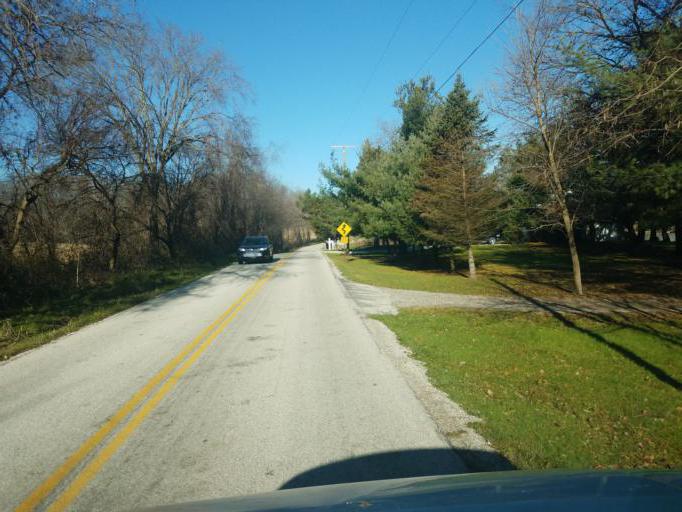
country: US
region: Ohio
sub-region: Richland County
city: Lincoln Heights
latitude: 40.7595
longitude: -82.3912
